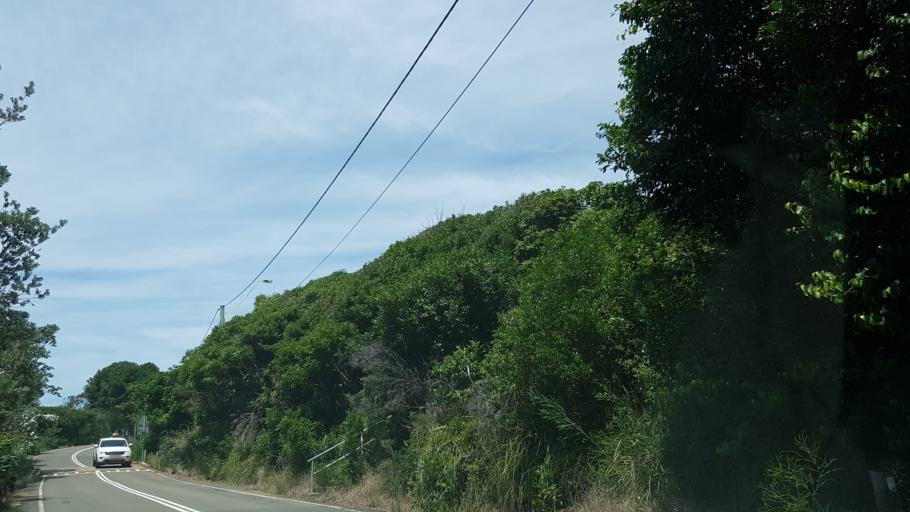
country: AU
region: New South Wales
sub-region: Pittwater
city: Bilgola Beach
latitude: -33.6466
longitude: 151.3260
